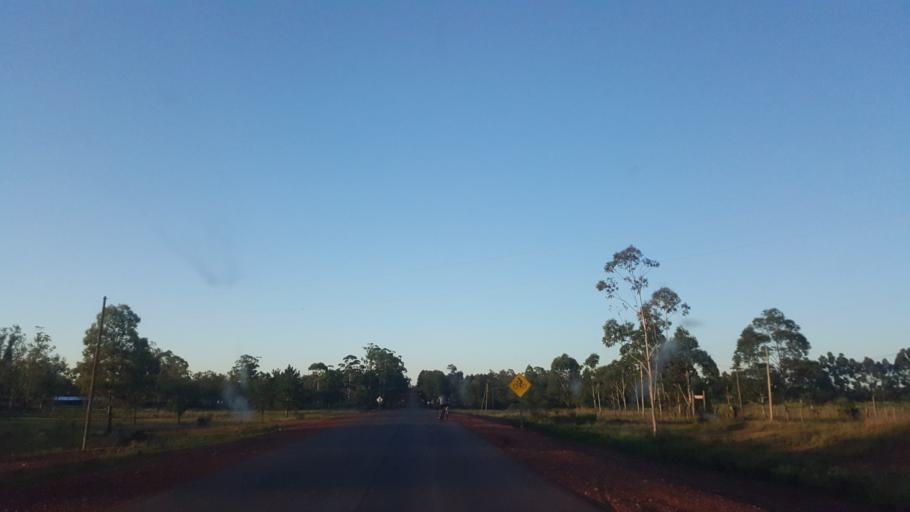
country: AR
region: Corrientes
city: Santo Tome
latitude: -28.5202
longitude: -56.0569
